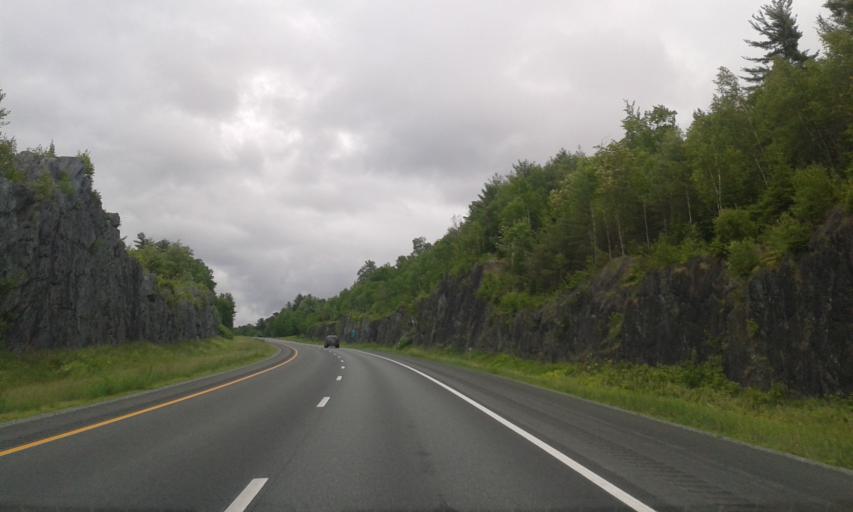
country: US
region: New Hampshire
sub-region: Grafton County
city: Littleton
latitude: 44.3130
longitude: -71.8522
